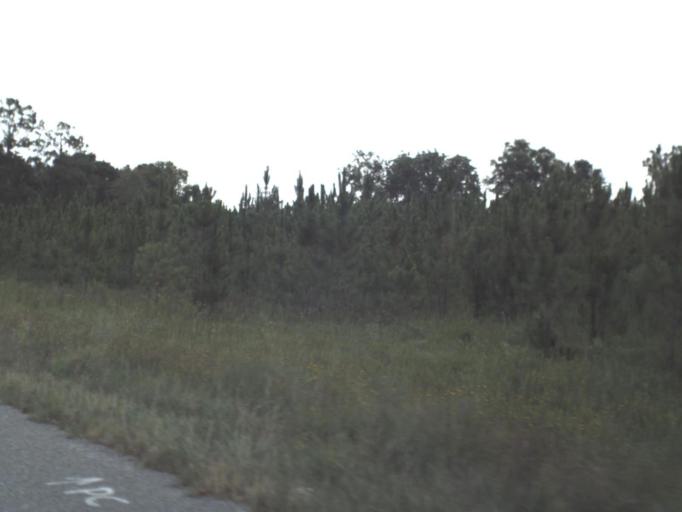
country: US
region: Florida
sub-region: Hamilton County
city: Jasper
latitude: 30.4904
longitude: -83.0845
